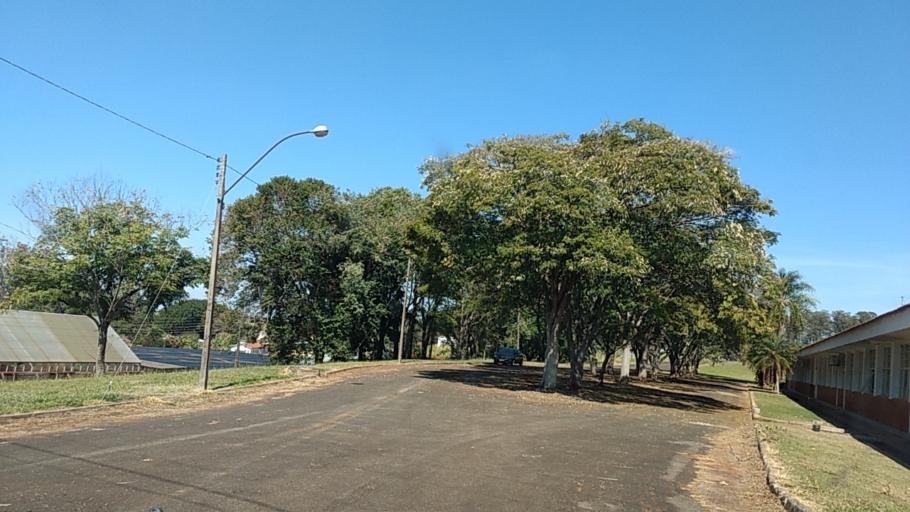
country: BR
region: Sao Paulo
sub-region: Botucatu
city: Botucatu
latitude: -22.8444
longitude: -48.4336
